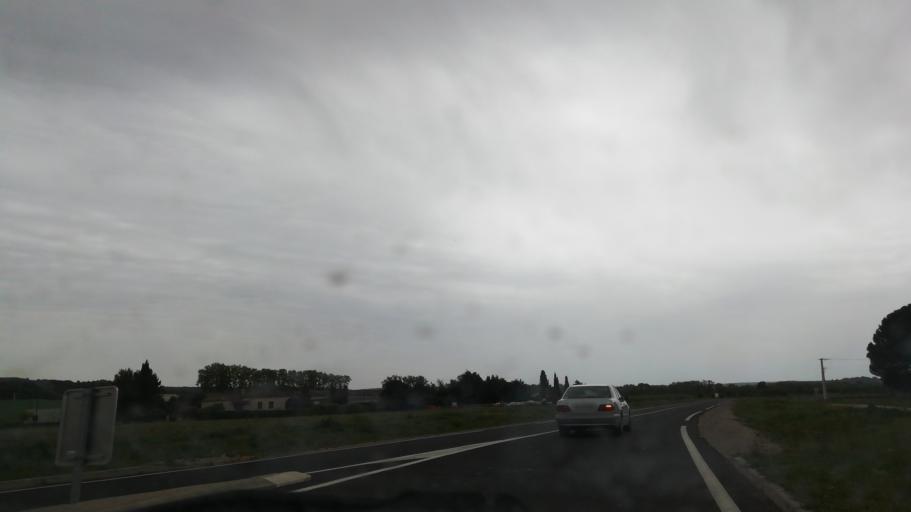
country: FR
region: Languedoc-Roussillon
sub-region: Departement de l'Herault
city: Aniane
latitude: 43.6826
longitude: 3.5760
